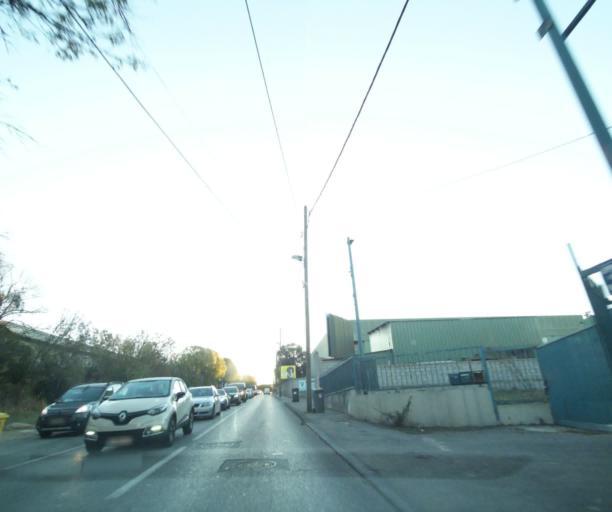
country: FR
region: Provence-Alpes-Cote d'Azur
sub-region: Departement des Bouches-du-Rhone
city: La Penne-sur-Huveaune
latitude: 43.2944
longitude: 5.4915
